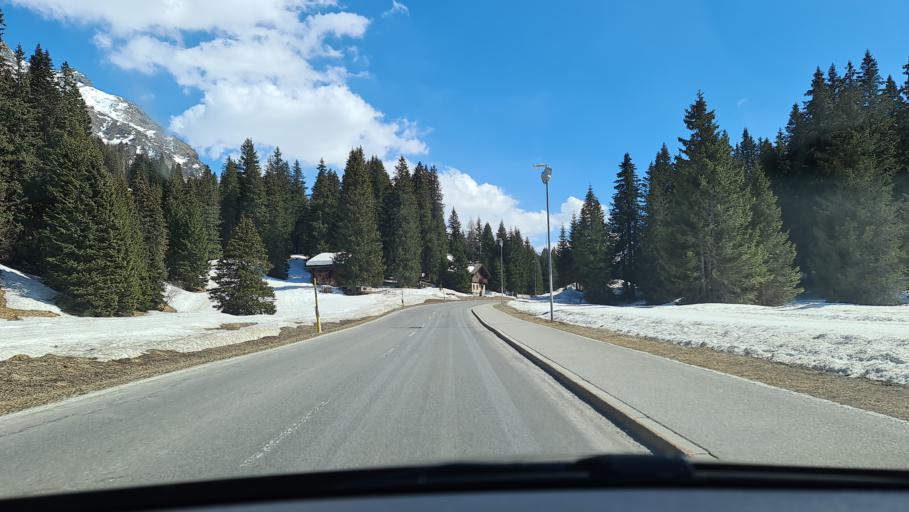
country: CH
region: Grisons
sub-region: Moesa District
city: Mesocco
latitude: 46.4560
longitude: 9.1971
